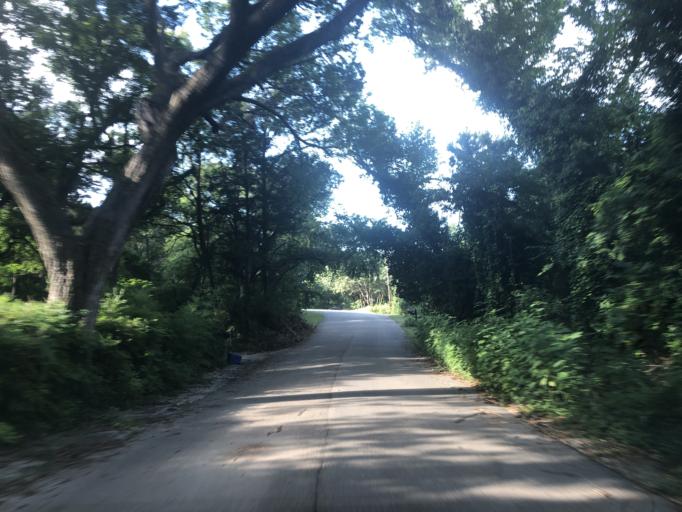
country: US
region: Texas
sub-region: Dallas County
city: Duncanville
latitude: 32.6658
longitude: -96.9219
